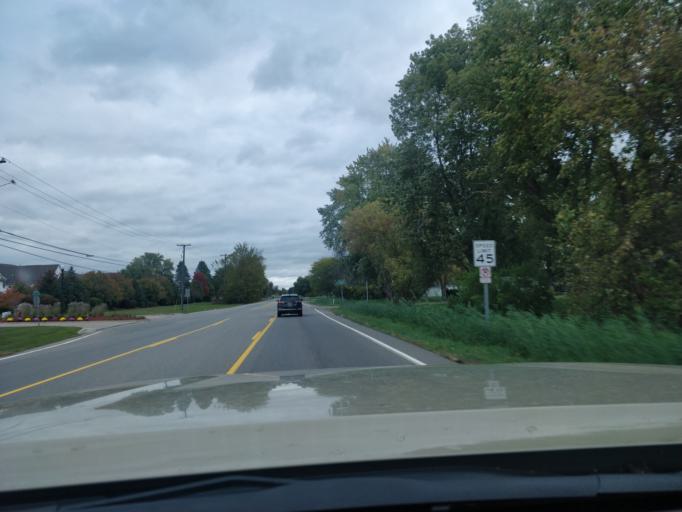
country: US
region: Michigan
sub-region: Wayne County
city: Taylor
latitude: 42.1810
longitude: -83.3239
